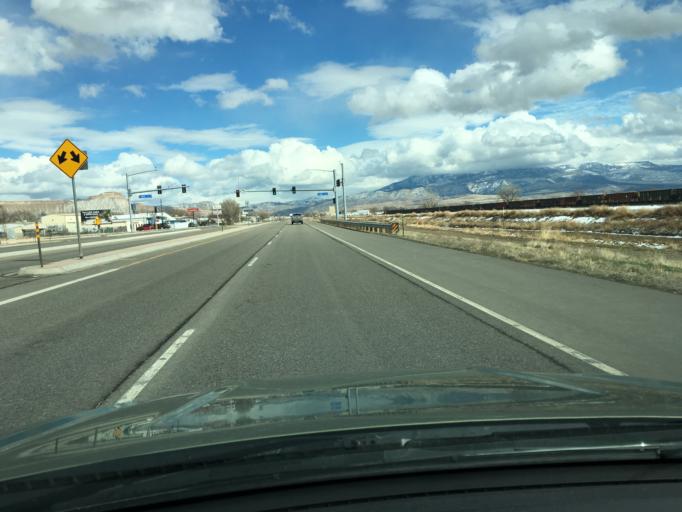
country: US
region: Colorado
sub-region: Mesa County
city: Fruitvale
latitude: 39.0730
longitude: -108.5144
